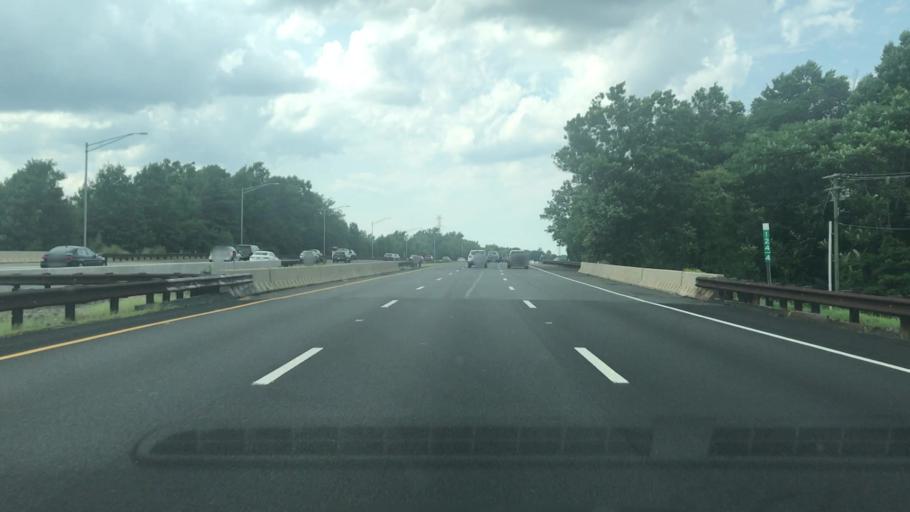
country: US
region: New Jersey
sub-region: Middlesex County
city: South Amboy
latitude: 40.4695
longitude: -74.2925
